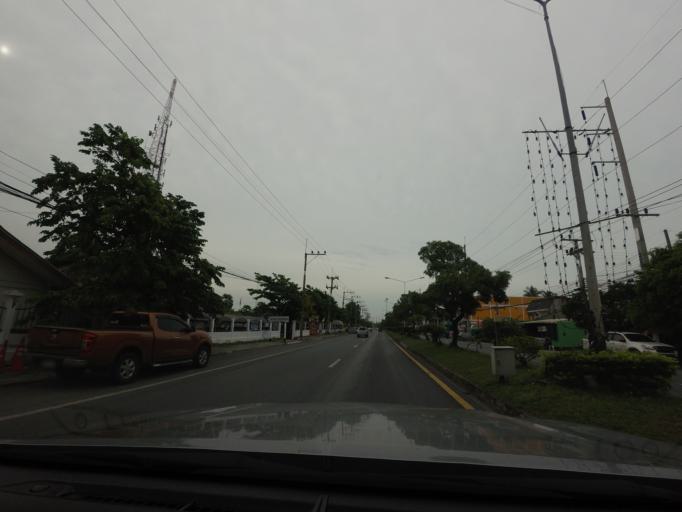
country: TH
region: Songkhla
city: Sathing Phra
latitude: 7.4718
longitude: 100.4397
